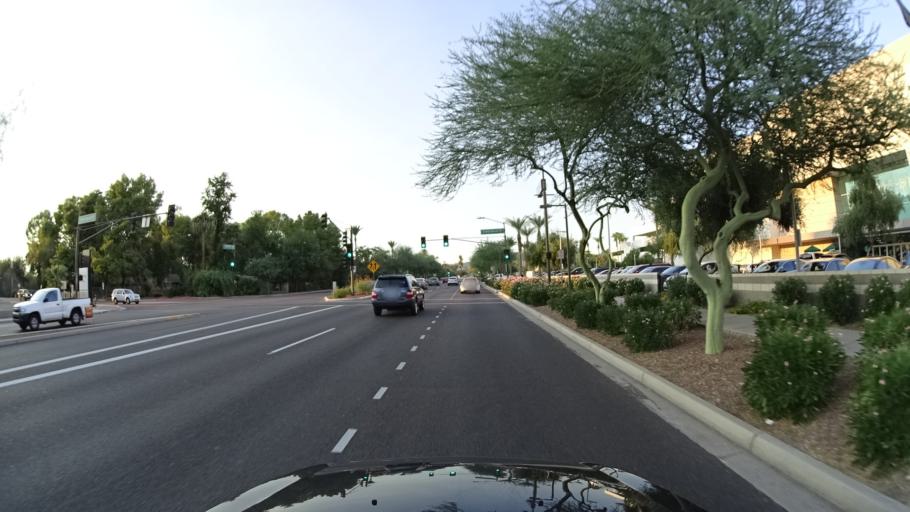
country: US
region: Arizona
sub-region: Maricopa County
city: Phoenix
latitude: 33.5106
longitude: -112.0301
